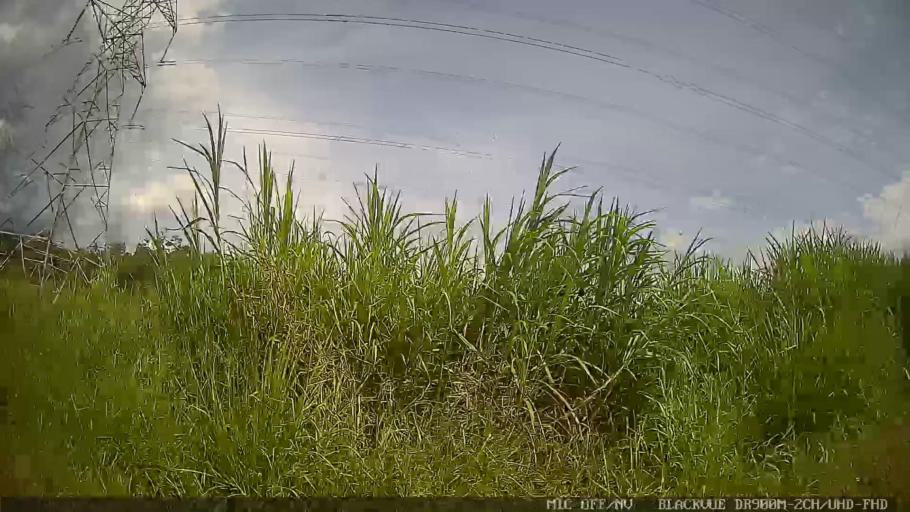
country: BR
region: Sao Paulo
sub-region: Mogi das Cruzes
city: Mogi das Cruzes
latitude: -23.6391
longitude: -46.2138
